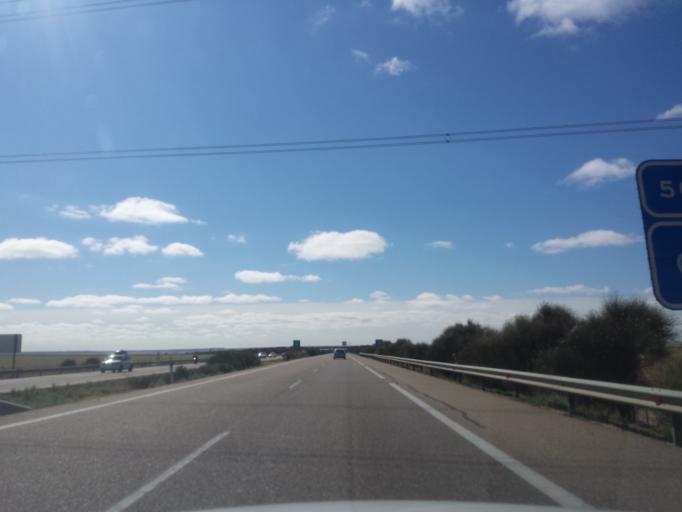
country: ES
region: Castille and Leon
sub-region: Provincia de Zamora
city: Quintanilla del Monte
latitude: 41.8059
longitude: -5.3515
